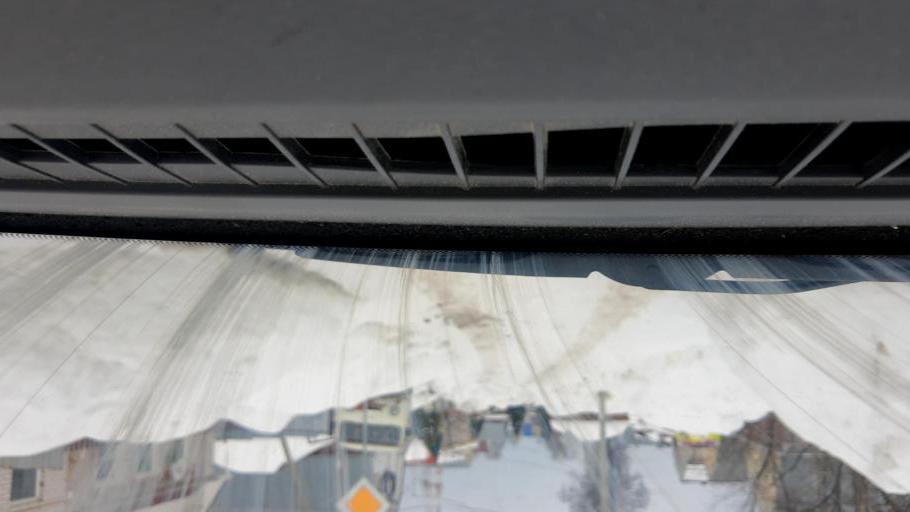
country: RU
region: Nizjnij Novgorod
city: Kstovo
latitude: 56.1375
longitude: 44.2099
